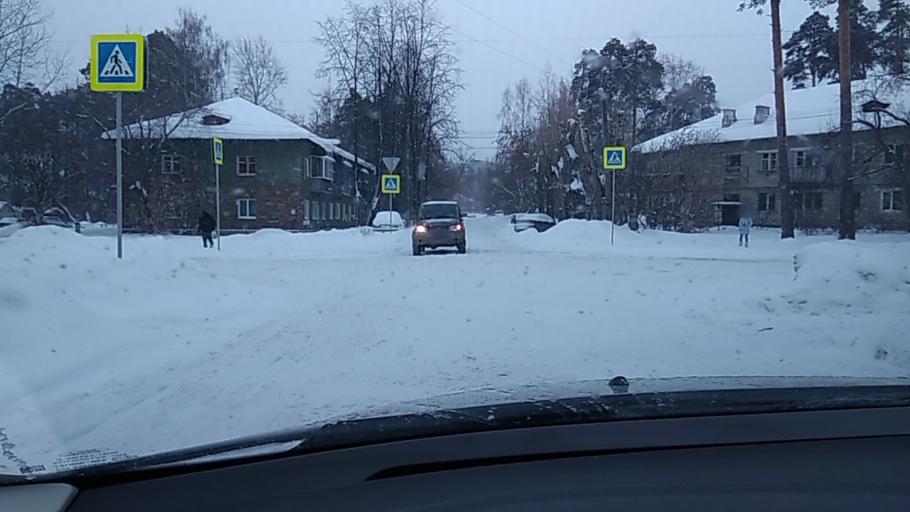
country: RU
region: Sverdlovsk
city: Sovkhoznyy
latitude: 56.8187
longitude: 60.5472
